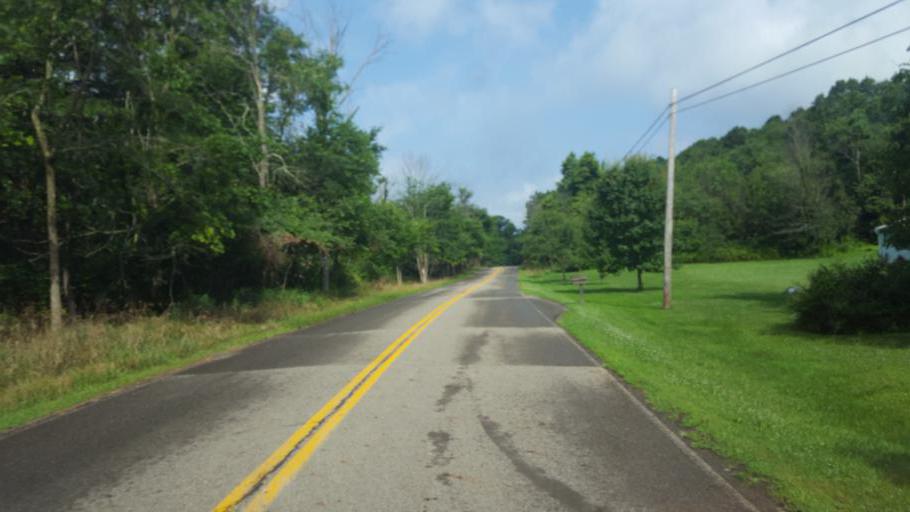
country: US
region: Ohio
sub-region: Columbiana County
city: Salineville
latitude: 40.5190
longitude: -80.8487
